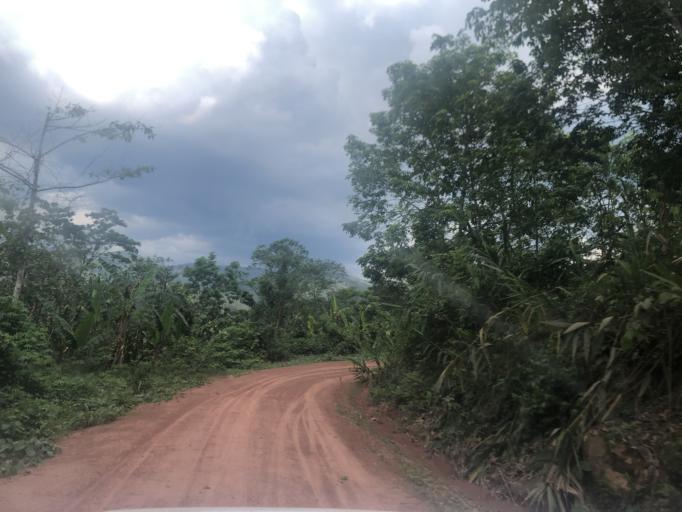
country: LA
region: Phongsali
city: Phongsali
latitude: 21.2940
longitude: 101.9906
